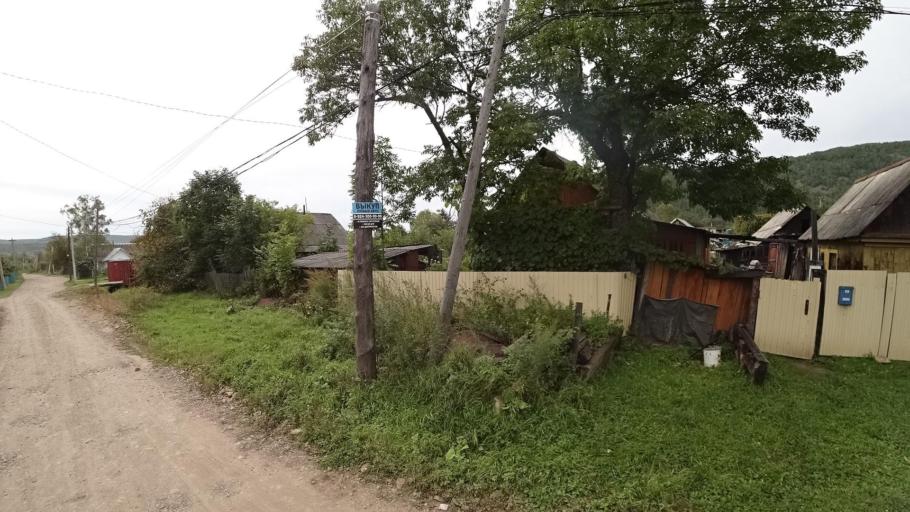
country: RU
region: Jewish Autonomous Oblast
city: Khingansk
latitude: 48.9948
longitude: 131.0550
